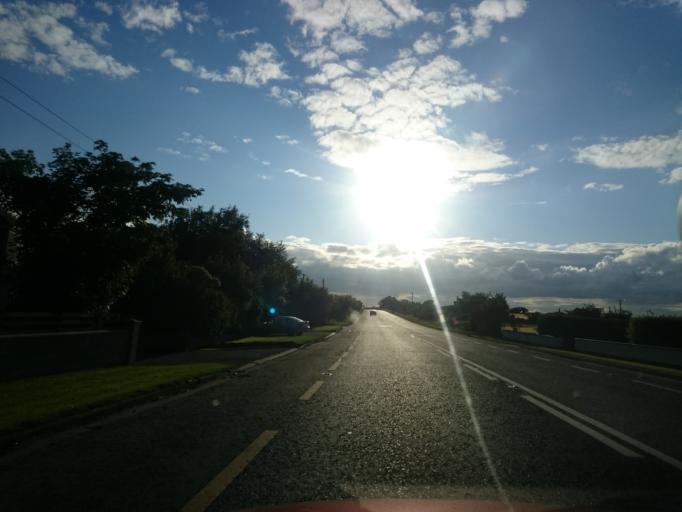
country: IE
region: Leinster
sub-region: Loch Garman
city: Ballygerry
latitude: 52.2438
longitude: -6.3616
